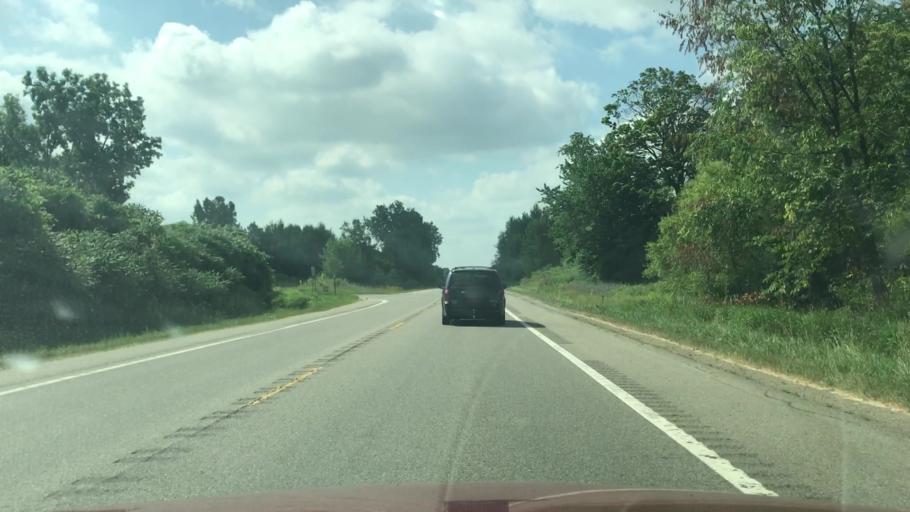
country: US
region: Michigan
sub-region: Kent County
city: Kent City
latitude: 43.2550
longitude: -85.8133
